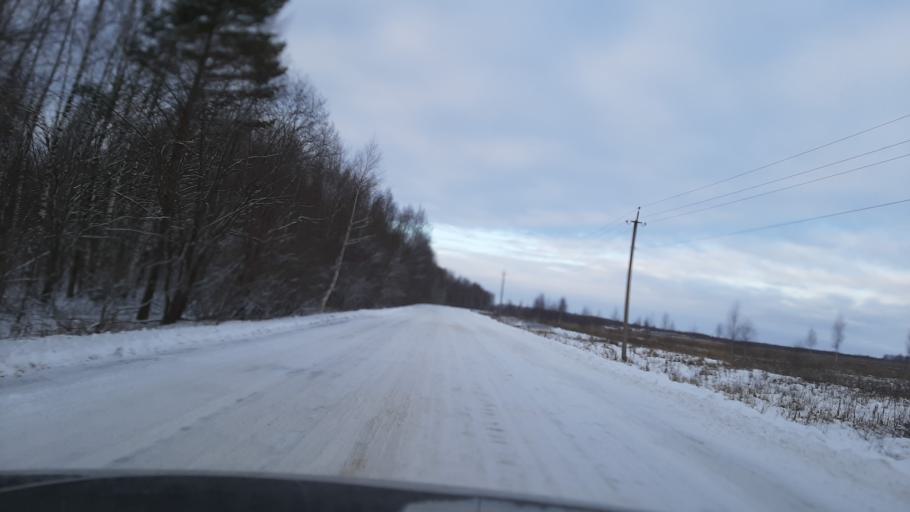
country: RU
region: Kostroma
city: Nerekhta
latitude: 57.4706
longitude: 40.6808
